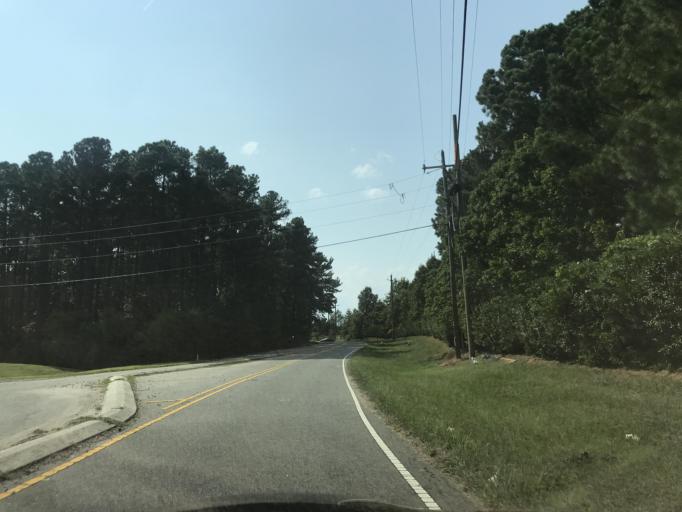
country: US
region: North Carolina
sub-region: Wake County
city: Morrisville
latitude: 35.8381
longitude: -78.8698
